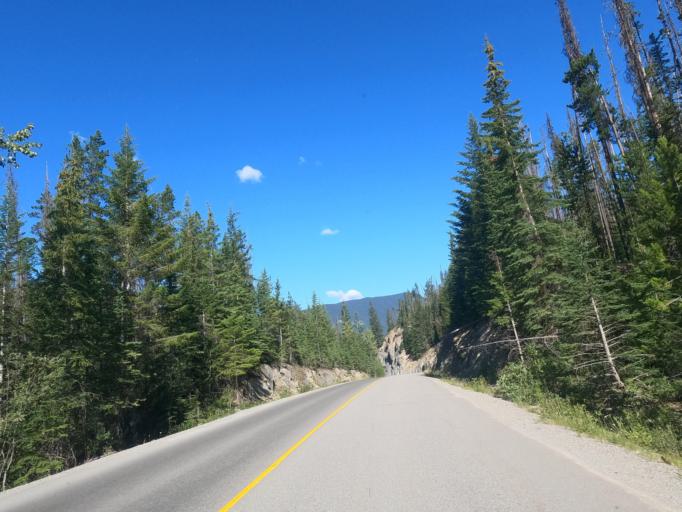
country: CA
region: Alberta
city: Lake Louise
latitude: 51.3802
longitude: -116.5187
